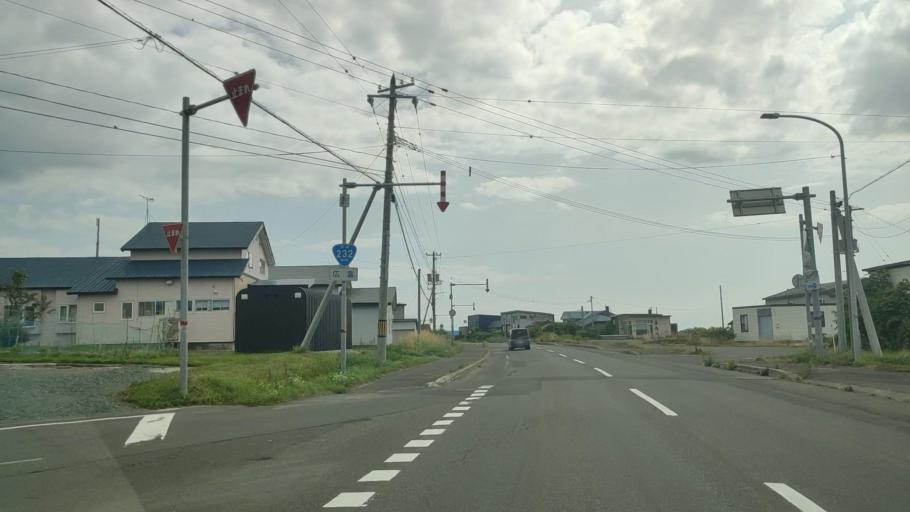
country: JP
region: Hokkaido
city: Rumoi
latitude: 44.1511
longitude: 141.6545
